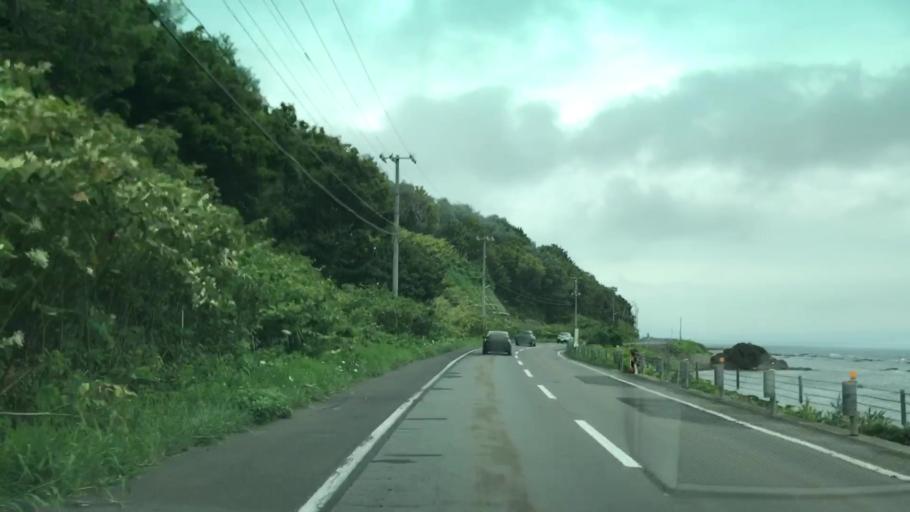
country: JP
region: Hokkaido
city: Iwanai
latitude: 42.8177
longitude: 140.3050
